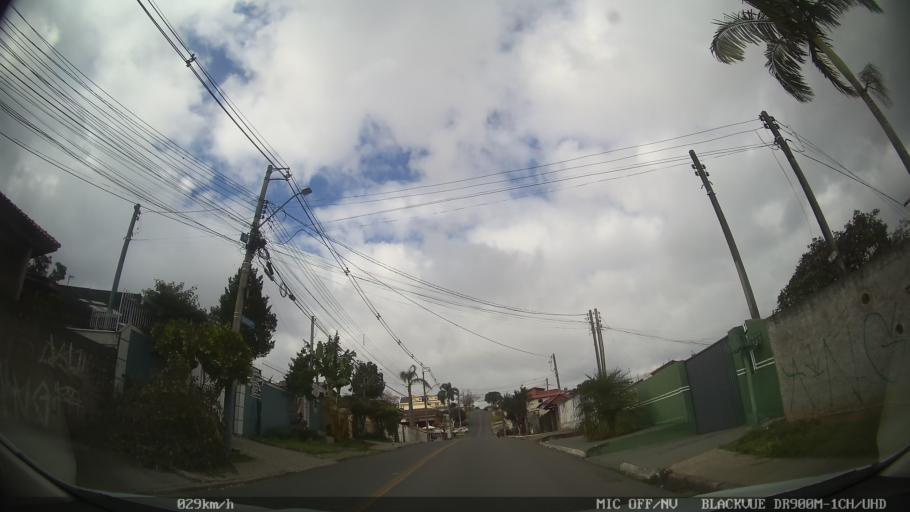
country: BR
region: Parana
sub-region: Almirante Tamandare
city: Almirante Tamandare
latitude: -25.3496
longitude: -49.2541
